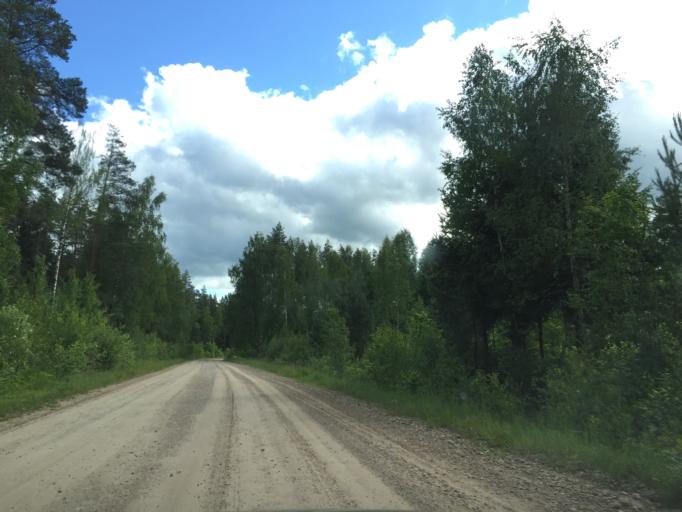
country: LV
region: Vecumnieki
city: Vecumnieki
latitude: 56.4940
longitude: 24.4084
